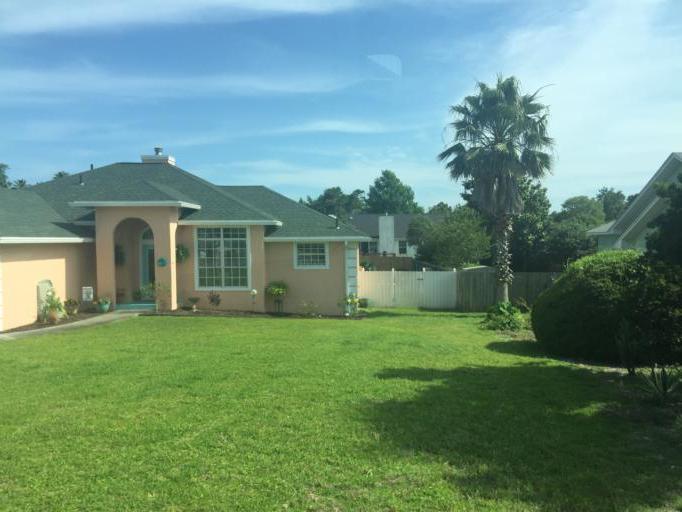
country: US
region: Florida
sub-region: Bay County
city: Laguna Beach
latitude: 30.2606
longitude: -85.9612
